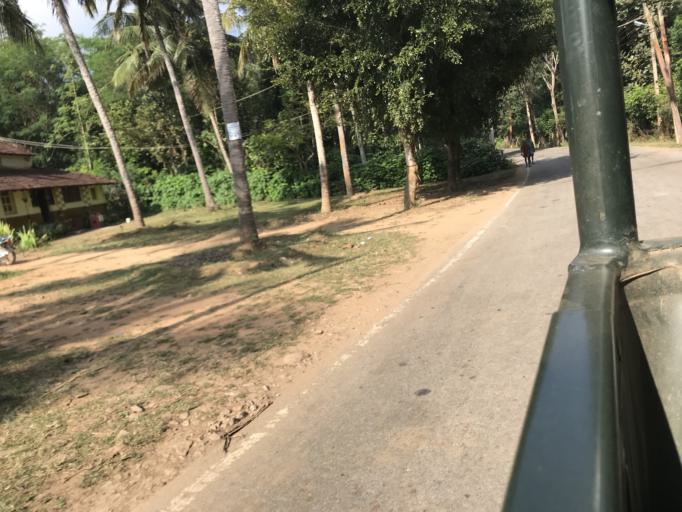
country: IN
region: Karnataka
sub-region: Mysore
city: Heggadadevankote
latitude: 11.9451
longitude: 76.2430
